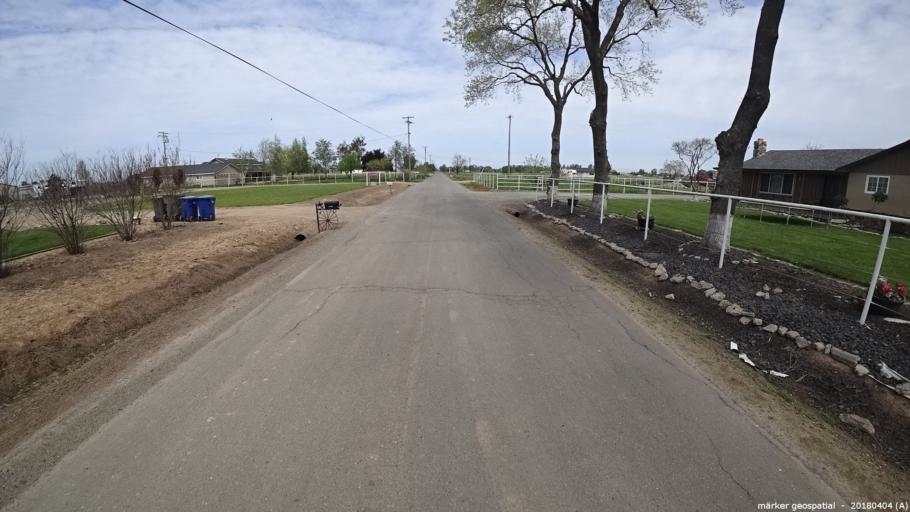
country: US
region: California
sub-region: Sacramento County
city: Herald
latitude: 38.2698
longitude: -121.2358
